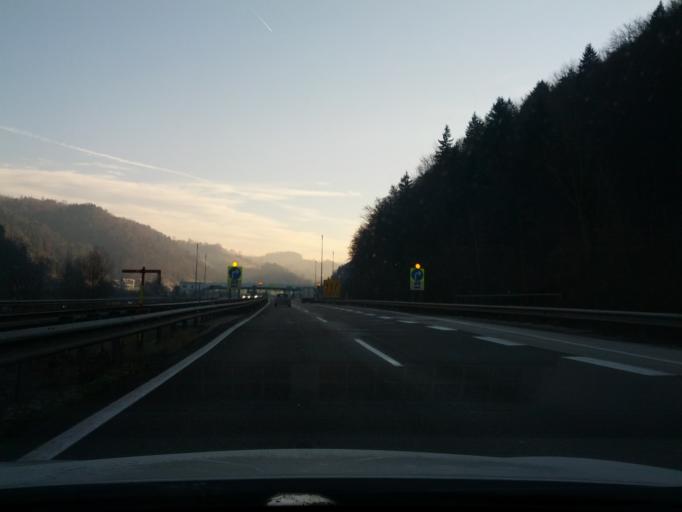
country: SI
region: Lukovica
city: Lukovica pri Domzalah
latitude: 46.1704
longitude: 14.7183
